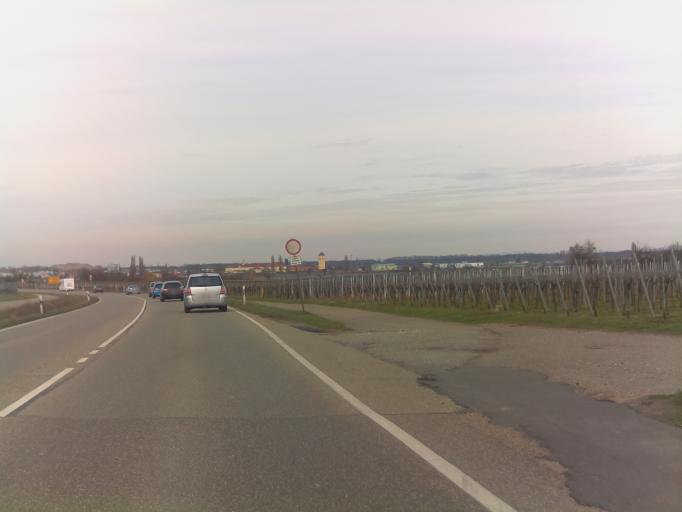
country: DE
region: Rheinland-Pfalz
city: Kirrweiler
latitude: 49.3253
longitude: 8.1505
